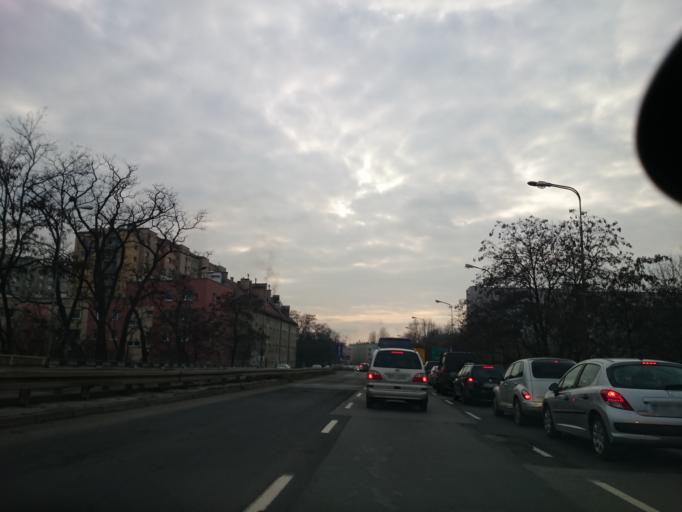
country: PL
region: Opole Voivodeship
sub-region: Powiat opolski
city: Opole
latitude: 50.6727
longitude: 17.9147
